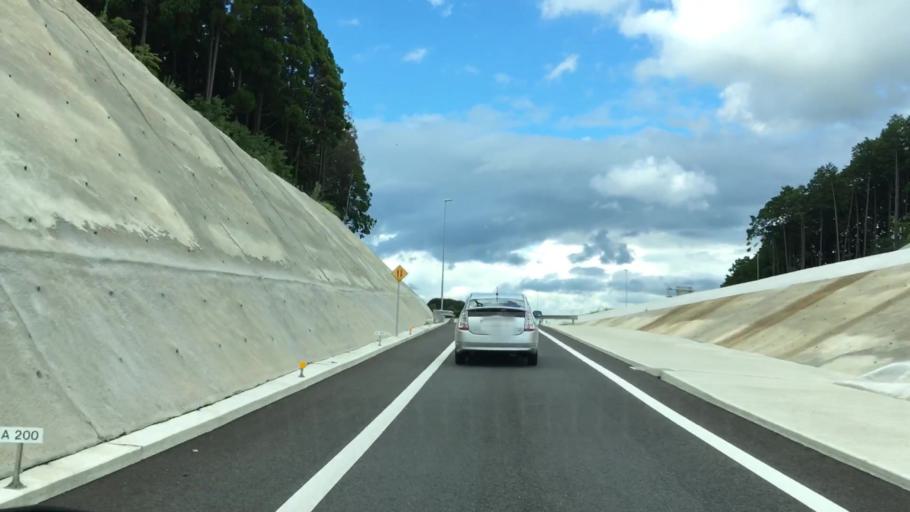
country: JP
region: Saga Prefecture
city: Imaricho-ko
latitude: 33.2971
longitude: 129.9121
